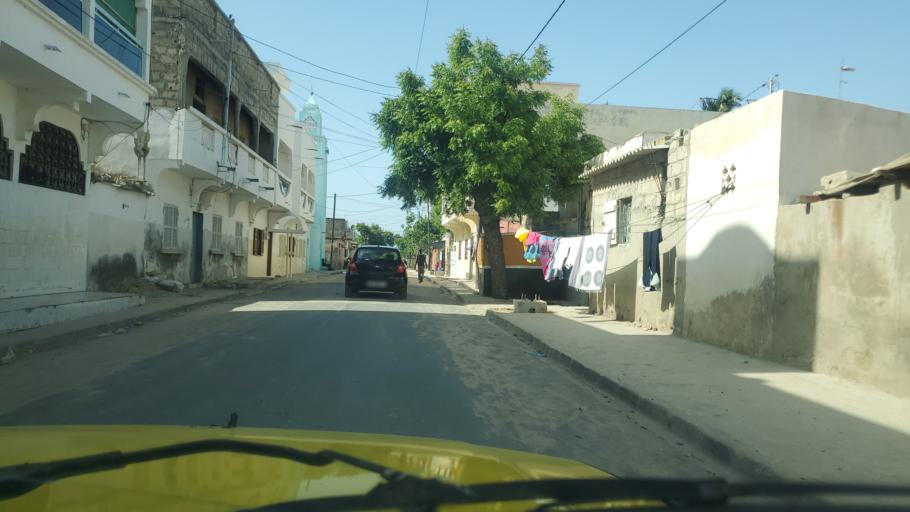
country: SN
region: Saint-Louis
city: Saint-Louis
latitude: 16.0204
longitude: -16.4856
